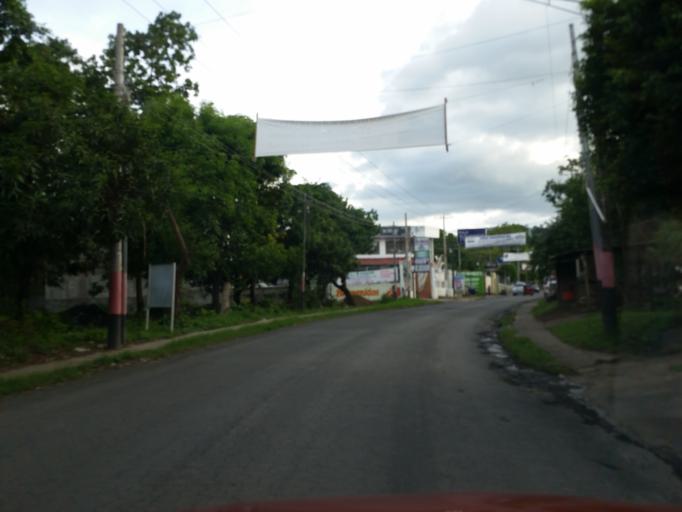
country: NI
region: Masaya
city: Ticuantepe
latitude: 12.0574
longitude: -86.1971
